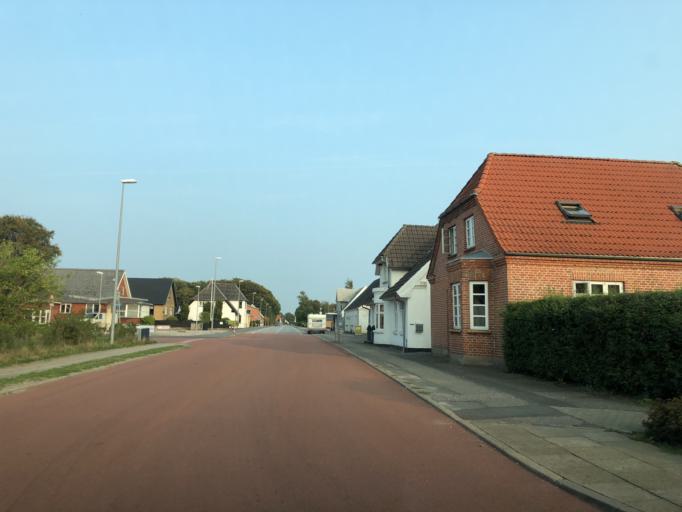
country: DK
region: South Denmark
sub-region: Billund Kommune
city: Billund
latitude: 55.8129
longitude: 9.0287
